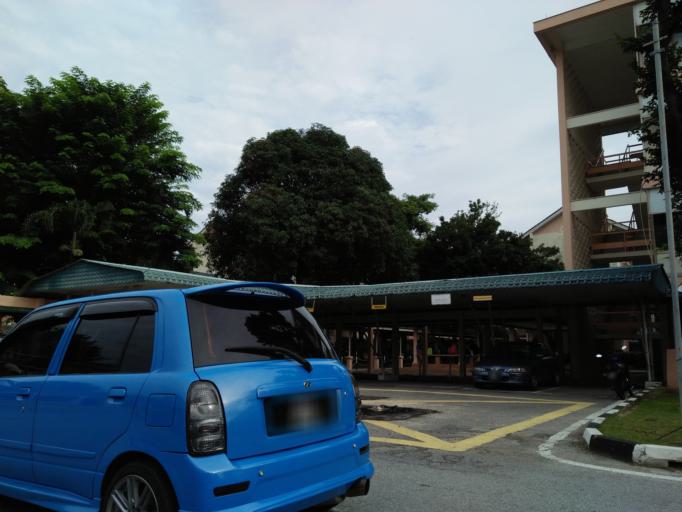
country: MY
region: Perak
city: Ipoh
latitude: 4.5880
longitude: 101.1252
